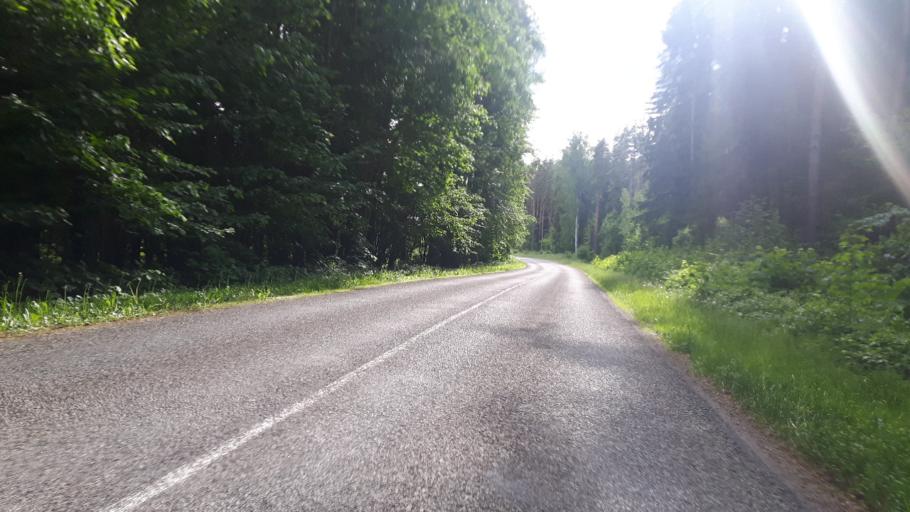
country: LV
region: Engure
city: Smarde
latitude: 56.9918
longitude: 23.3107
